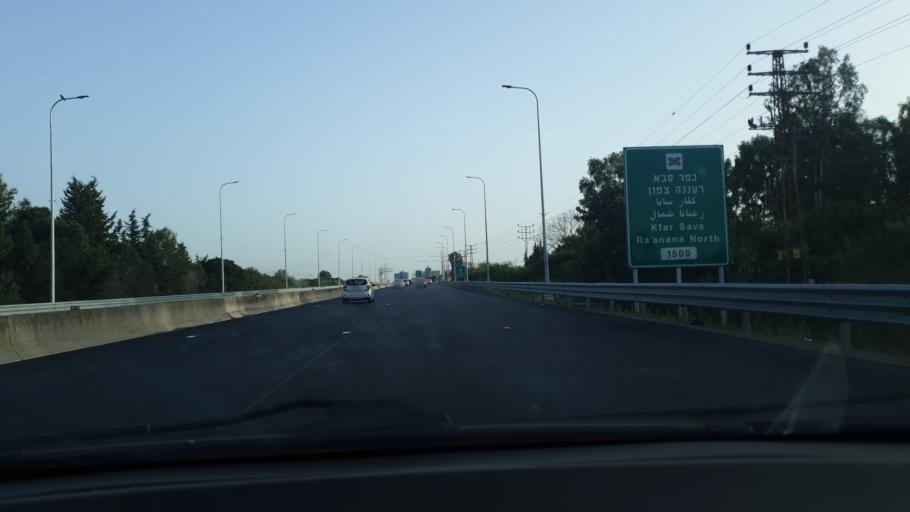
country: IL
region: Central District
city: Ra'anana
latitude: 32.2136
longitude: 34.8835
